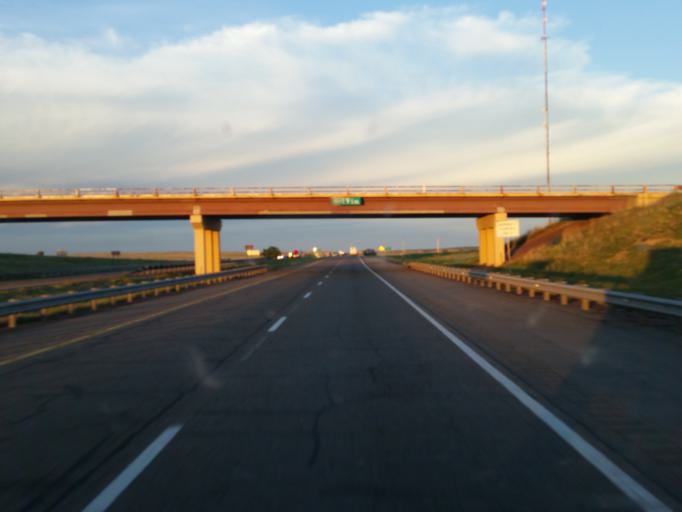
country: US
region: New Mexico
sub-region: San Miguel County
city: Las Vegas
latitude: 34.9914
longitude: -105.2943
